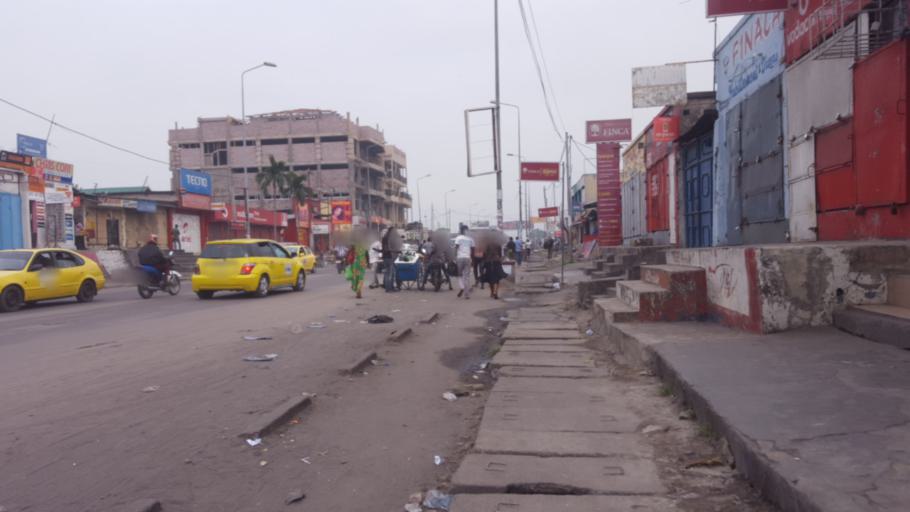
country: CD
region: Kinshasa
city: Kinshasa
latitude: -4.3405
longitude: 15.3130
